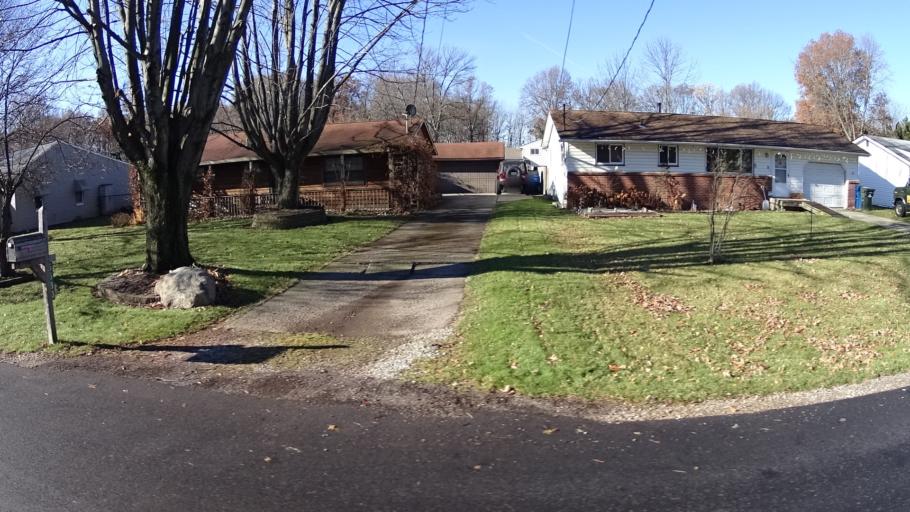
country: US
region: Ohio
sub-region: Lorain County
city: North Ridgeville
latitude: 41.4090
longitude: -81.9985
